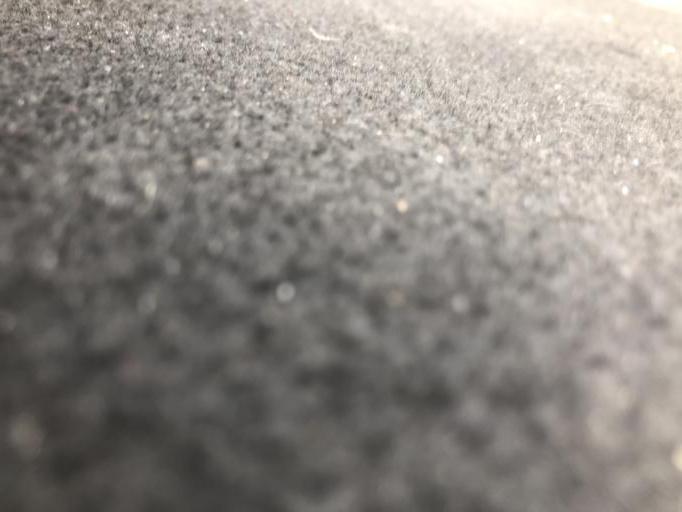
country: CL
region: Santiago Metropolitan
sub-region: Provincia de Cordillera
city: Puente Alto
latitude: -33.6111
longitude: -70.5214
